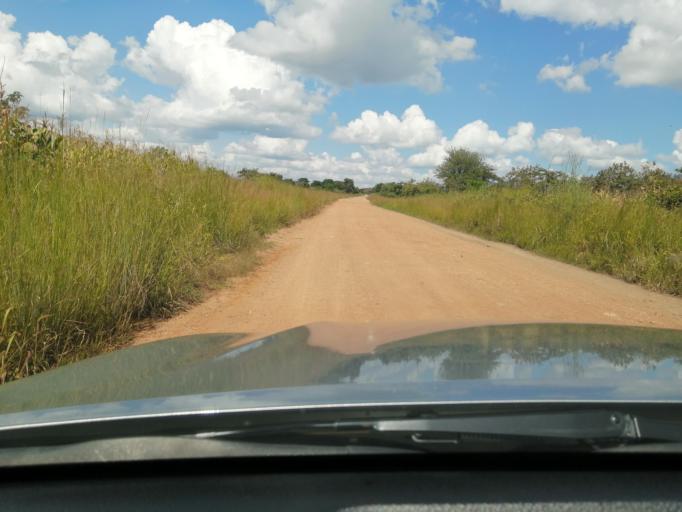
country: ZM
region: Lusaka
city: Lusaka
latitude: -15.2004
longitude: 28.0409
